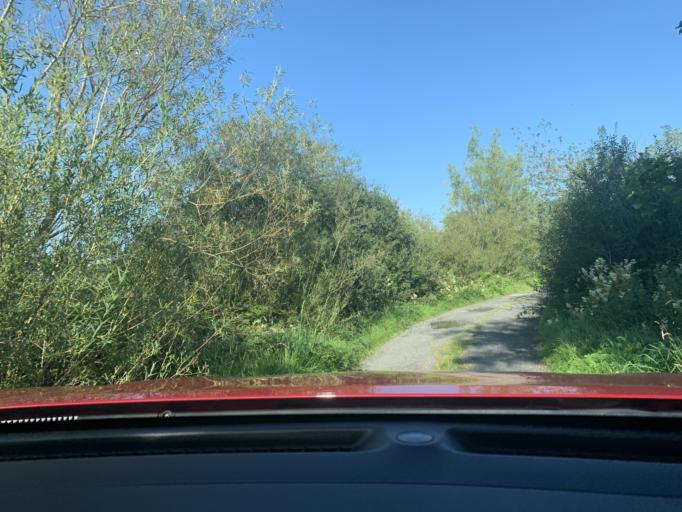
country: IE
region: Connaught
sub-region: Sligo
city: Tobercurry
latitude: 54.0650
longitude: -8.7892
